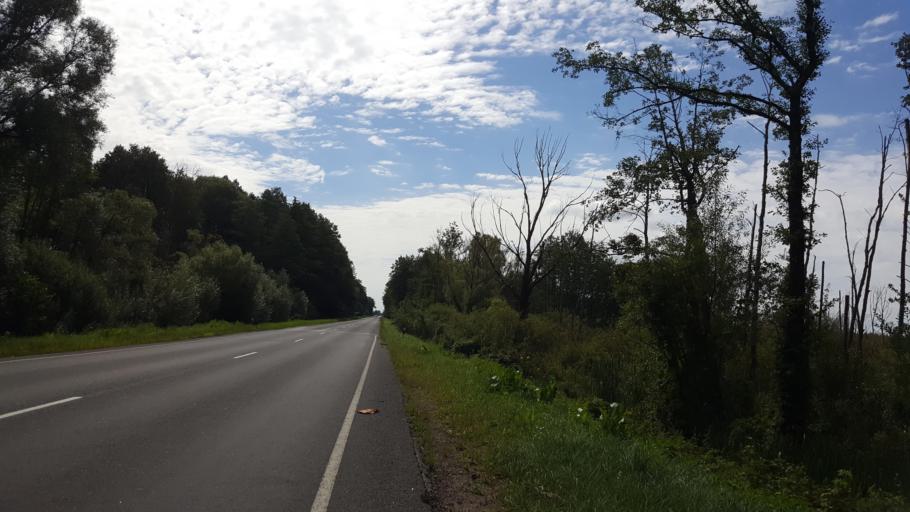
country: BY
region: Brest
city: Zhabinka
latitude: 52.2711
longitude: 23.9552
